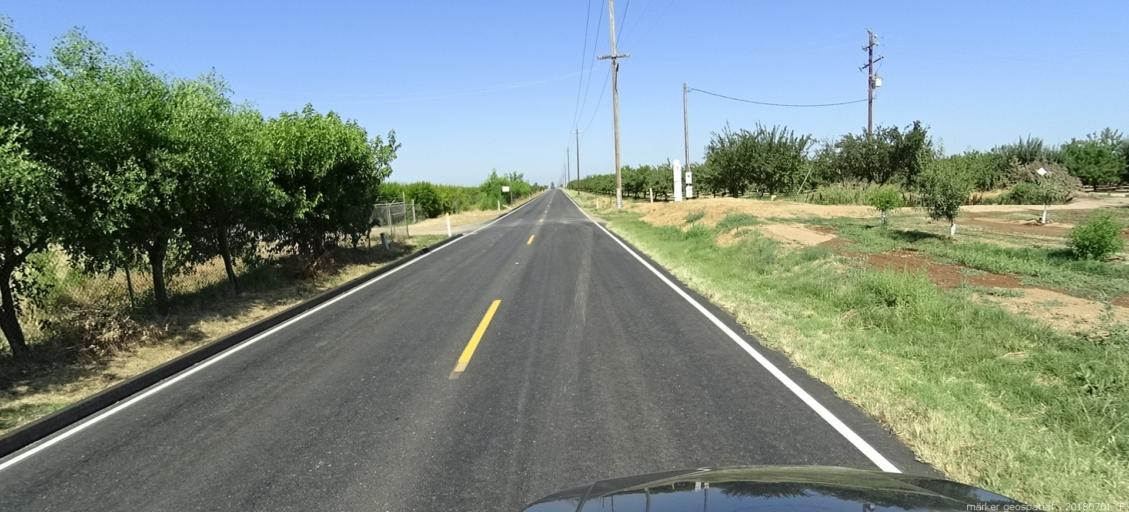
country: US
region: California
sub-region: Madera County
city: Bonadelle Ranchos-Madera Ranchos
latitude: 36.8804
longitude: -119.8702
